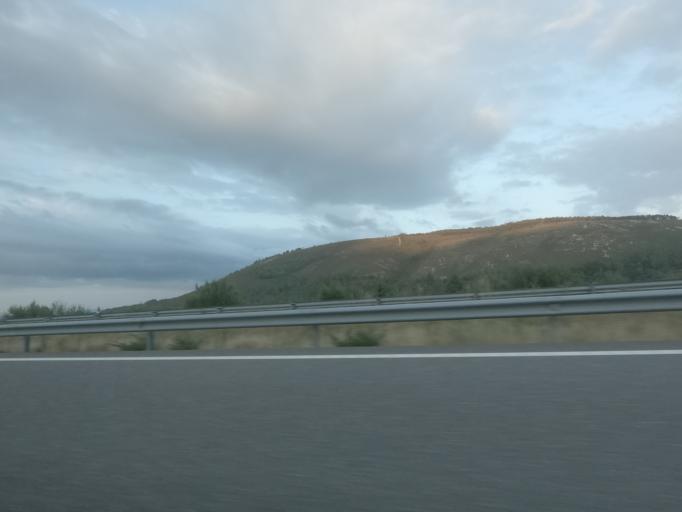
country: ES
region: Galicia
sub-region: Provincia de Ourense
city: Melon
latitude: 42.2436
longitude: -8.2275
